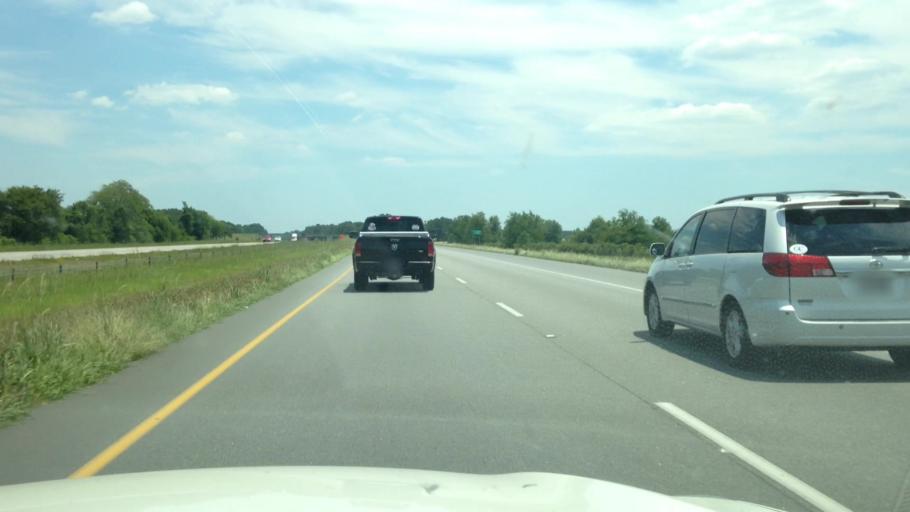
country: US
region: South Carolina
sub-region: Lee County
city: Bishopville
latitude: 34.1861
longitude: -80.2211
